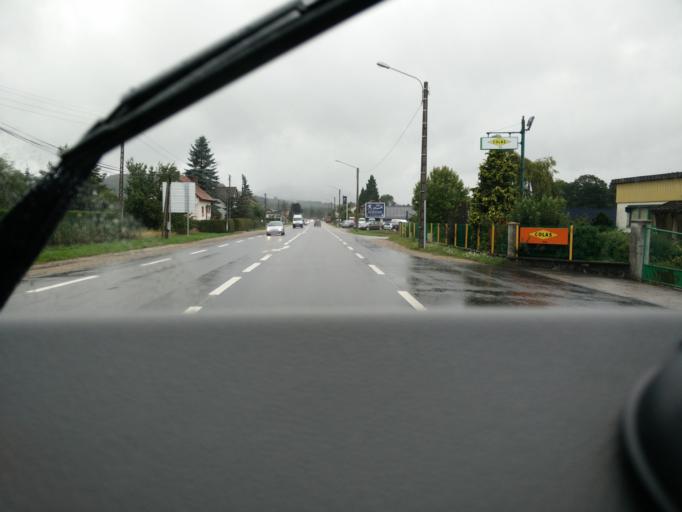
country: FR
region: Lorraine
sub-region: Departement des Vosges
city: Saint-Leonard
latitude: 48.2075
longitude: 6.9437
